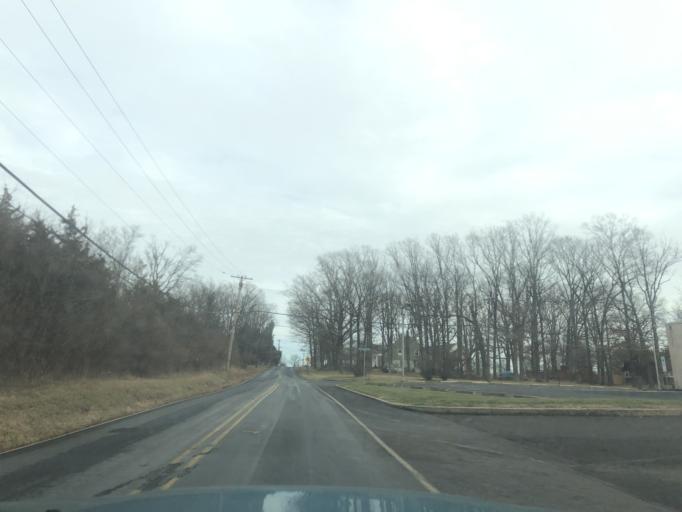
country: US
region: Pennsylvania
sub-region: Montgomery County
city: Harleysville
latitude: 40.2759
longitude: -75.4058
